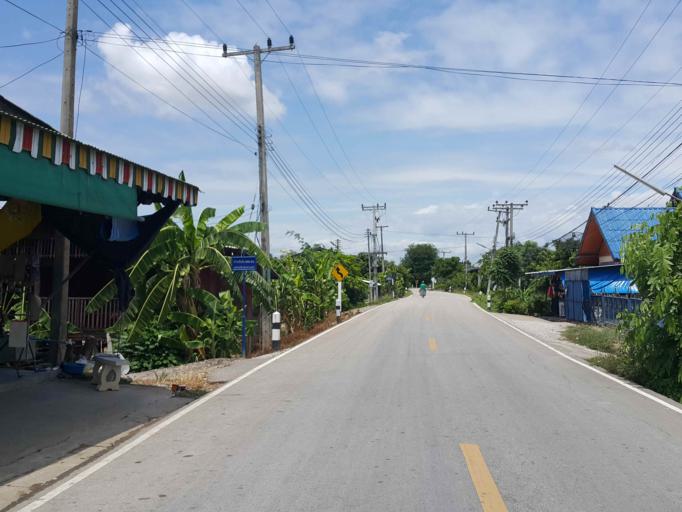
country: TH
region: Lamphun
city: Pa Sang
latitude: 18.5263
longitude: 98.8957
